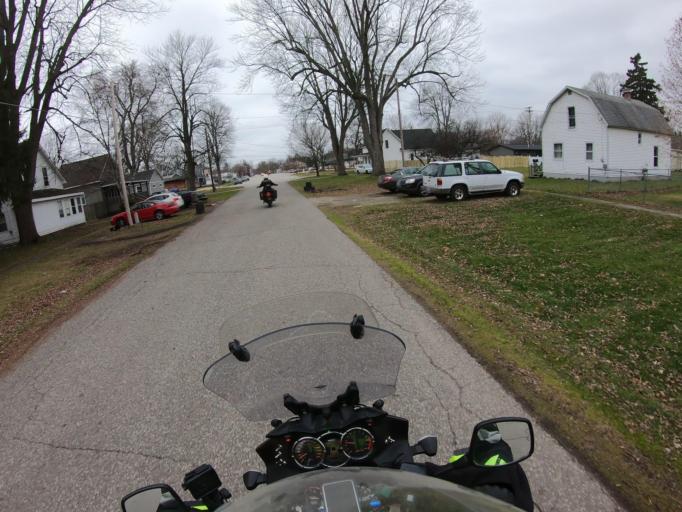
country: US
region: Michigan
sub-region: Saginaw County
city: Saint Charles
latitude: 43.2988
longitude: -84.1381
